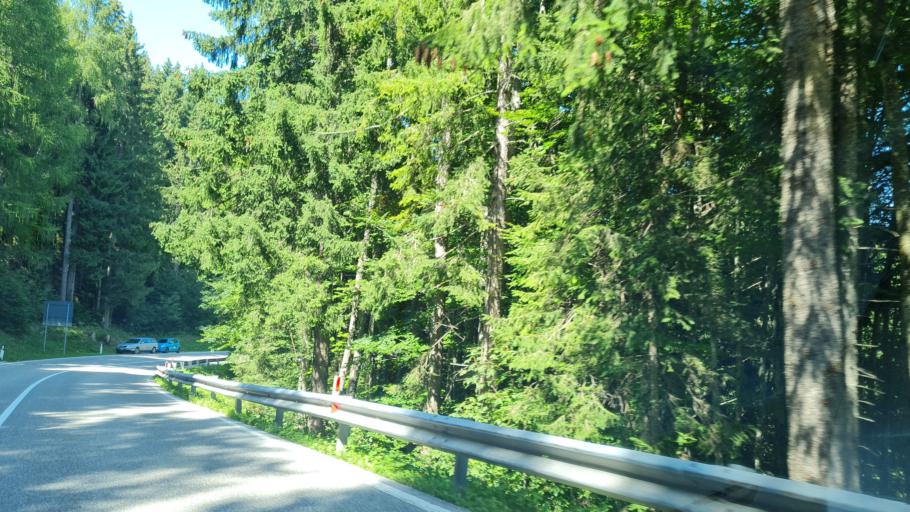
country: IT
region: Trentino-Alto Adige
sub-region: Provincia di Trento
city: Folgaria
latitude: 45.9211
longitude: 11.2076
